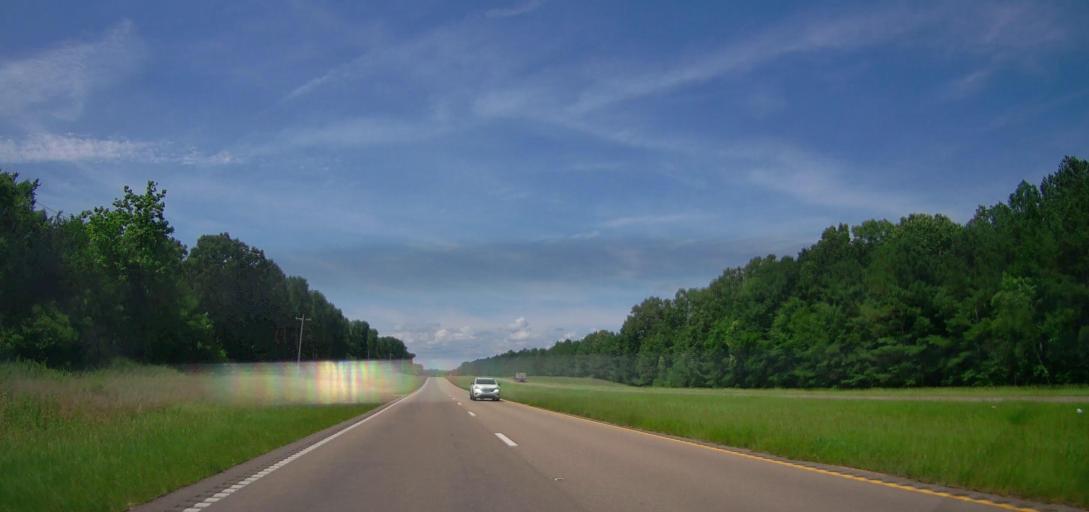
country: US
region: Mississippi
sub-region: Monroe County
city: Aberdeen
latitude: 33.9153
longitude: -88.5962
